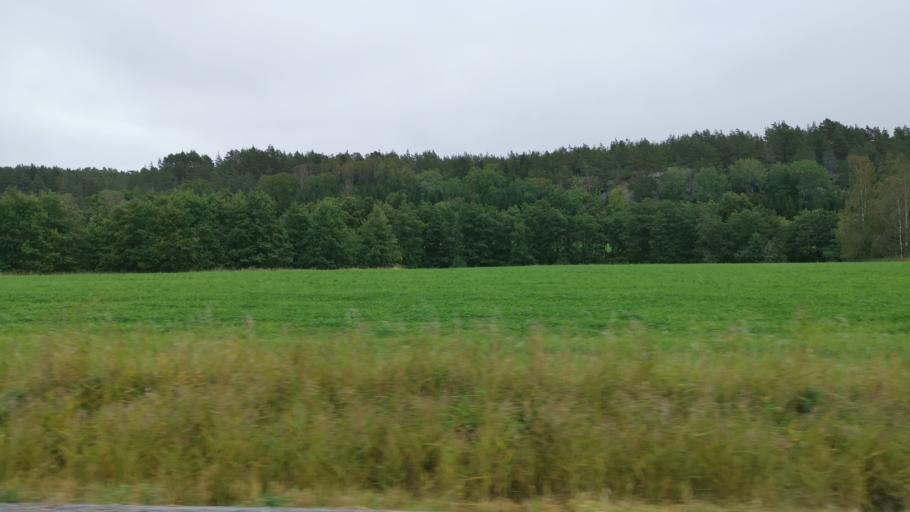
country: SE
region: Vaestra Goetaland
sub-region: Tanums Kommun
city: Tanumshede
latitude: 58.6318
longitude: 11.3468
